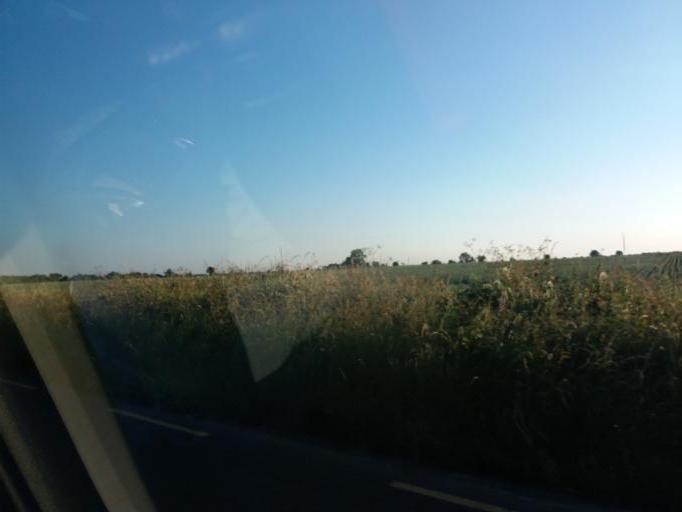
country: IE
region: Leinster
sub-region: An Mhi
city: Ashbourne
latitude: 53.5257
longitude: -6.3596
